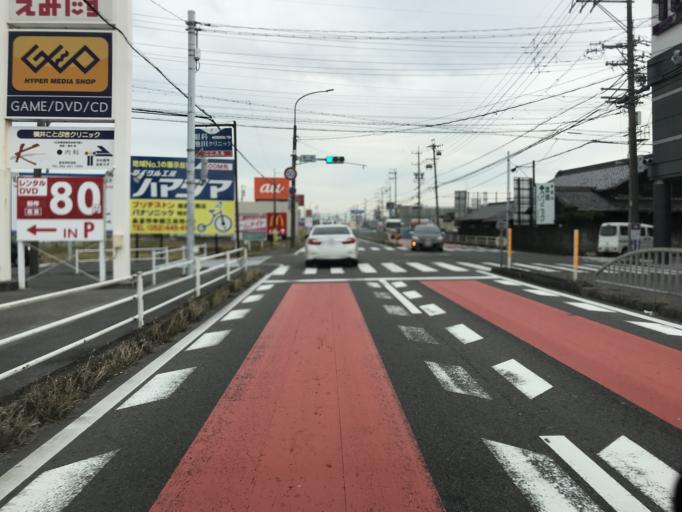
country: JP
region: Aichi
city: Kanie
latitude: 35.1841
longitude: 136.8274
